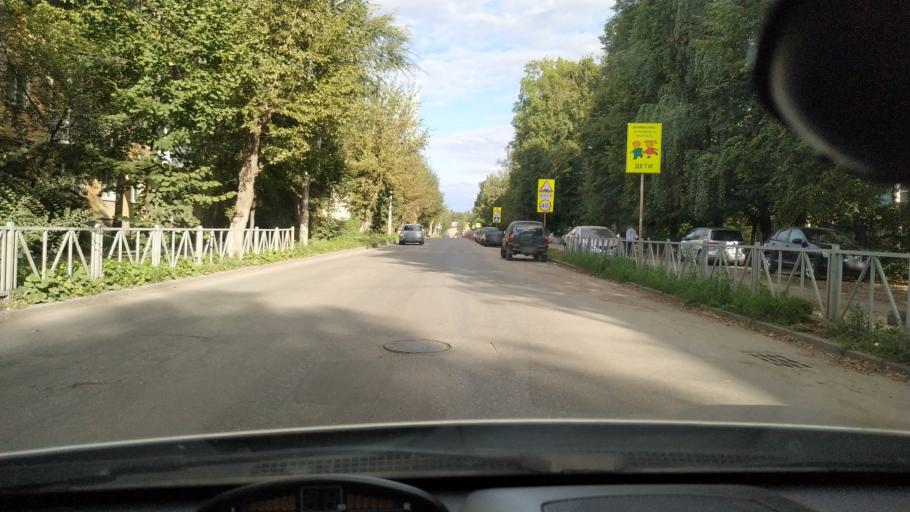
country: RU
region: Rjazan
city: Ryazan'
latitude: 54.6057
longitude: 39.7146
